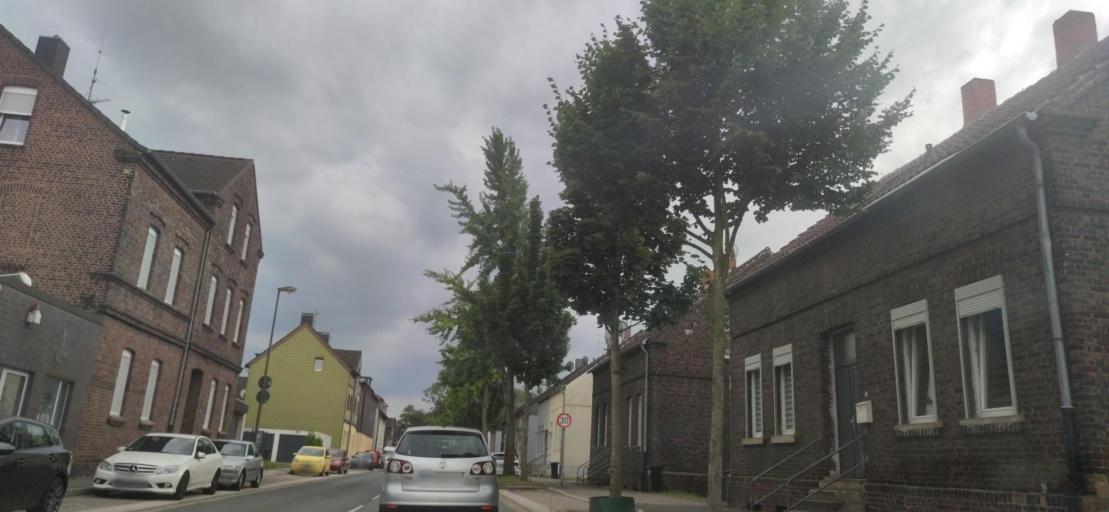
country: DE
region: North Rhine-Westphalia
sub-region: Regierungsbezirk Dusseldorf
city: Essen
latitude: 51.5073
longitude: 7.0497
